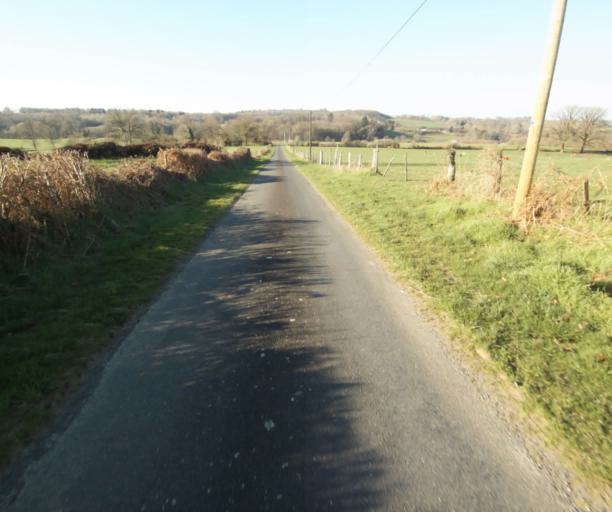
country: FR
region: Limousin
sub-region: Departement de la Correze
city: Uzerche
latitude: 45.3819
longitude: 1.5859
